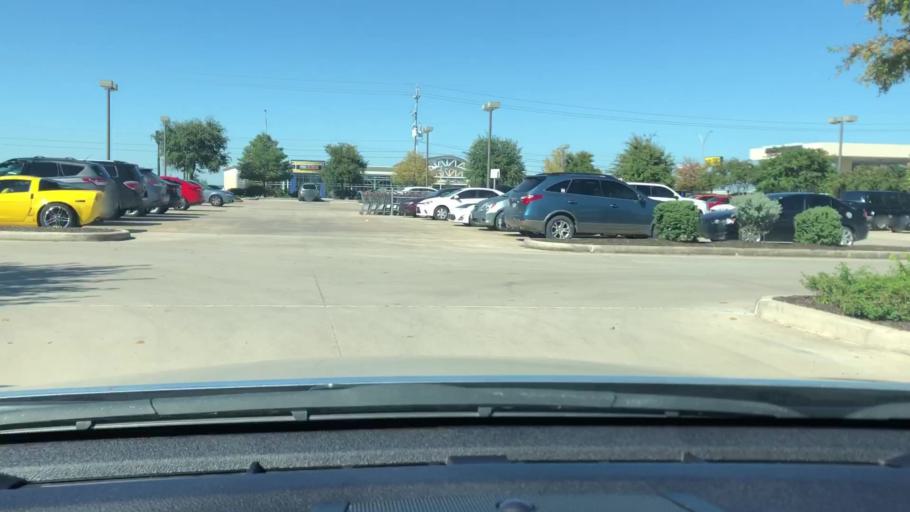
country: US
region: Texas
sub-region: Bexar County
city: Selma
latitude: 29.5771
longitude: -98.3185
